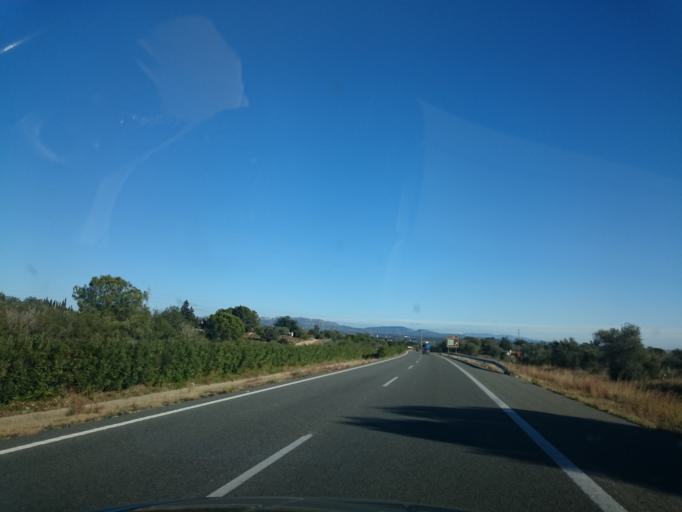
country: ES
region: Catalonia
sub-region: Provincia de Tarragona
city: Masdenverge
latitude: 40.7086
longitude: 0.5526
